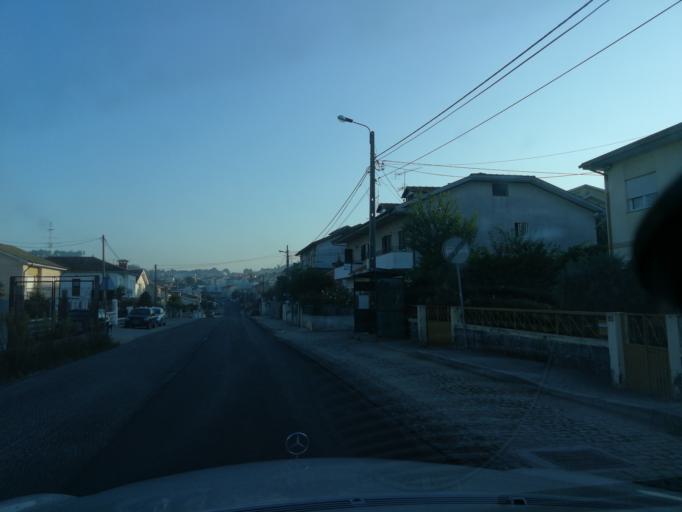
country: PT
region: Braga
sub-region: Braga
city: Braga
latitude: 41.5241
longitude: -8.4302
